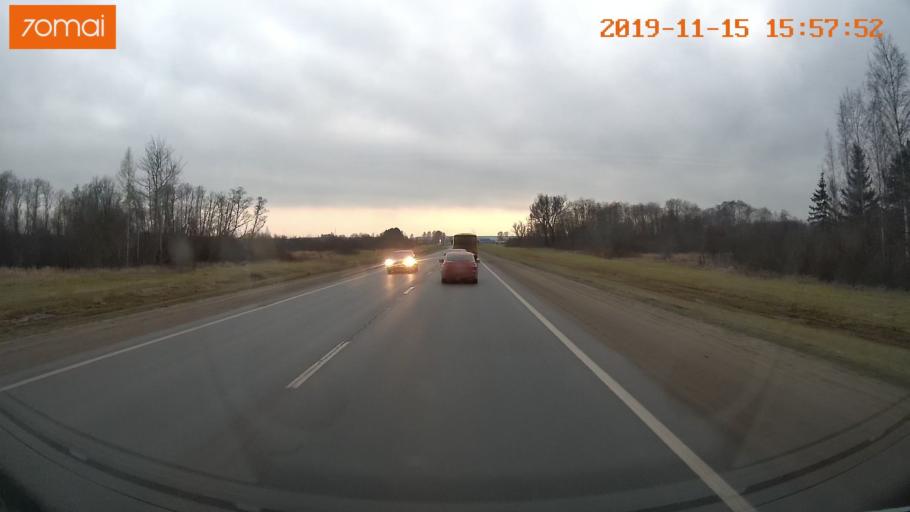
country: RU
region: Jaroslavl
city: Yaroslavl
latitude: 57.8259
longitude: 39.9597
